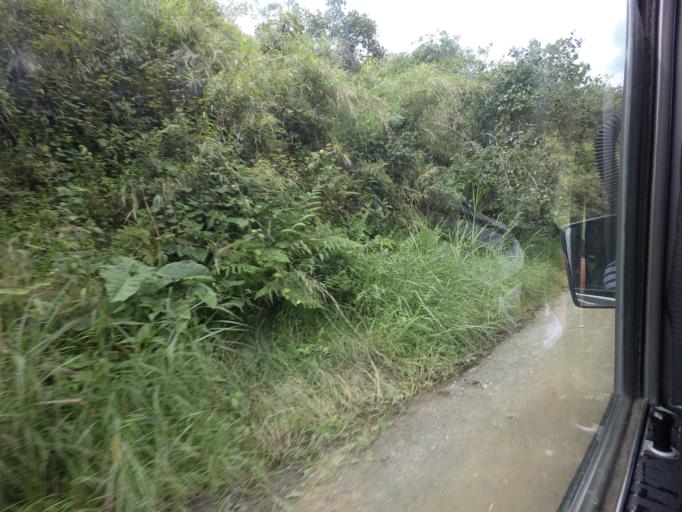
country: CO
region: Huila
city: Isnos
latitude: 1.9573
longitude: -76.2837
